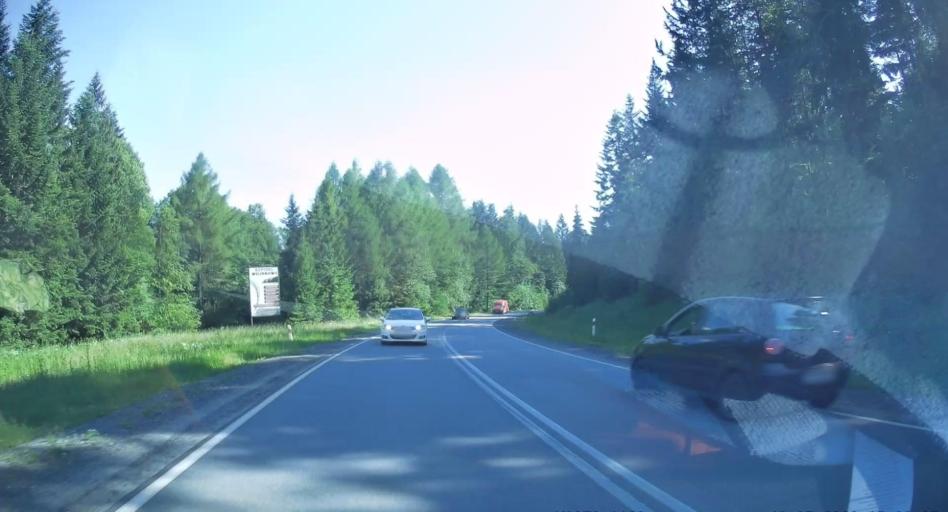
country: PL
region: Lesser Poland Voivodeship
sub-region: Powiat nowosadecki
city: Krynica-Zdroj
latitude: 49.4599
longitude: 20.9576
